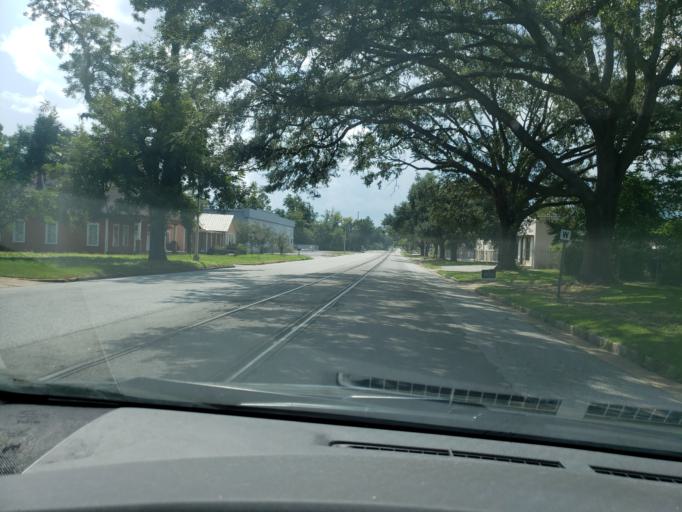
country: US
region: Georgia
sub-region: Dougherty County
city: Albany
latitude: 31.5816
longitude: -84.1594
